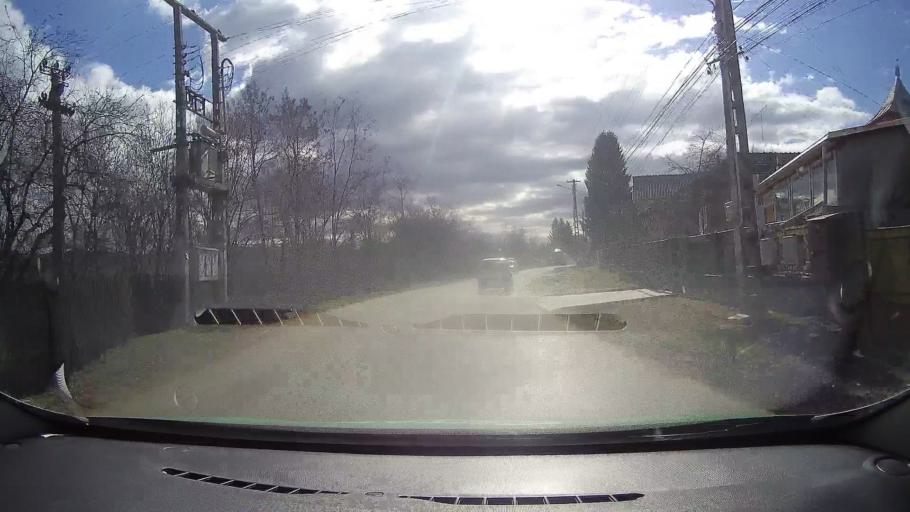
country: RO
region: Dambovita
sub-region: Oras Pucioasa
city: Pucioasa
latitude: 45.0630
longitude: 25.4250
